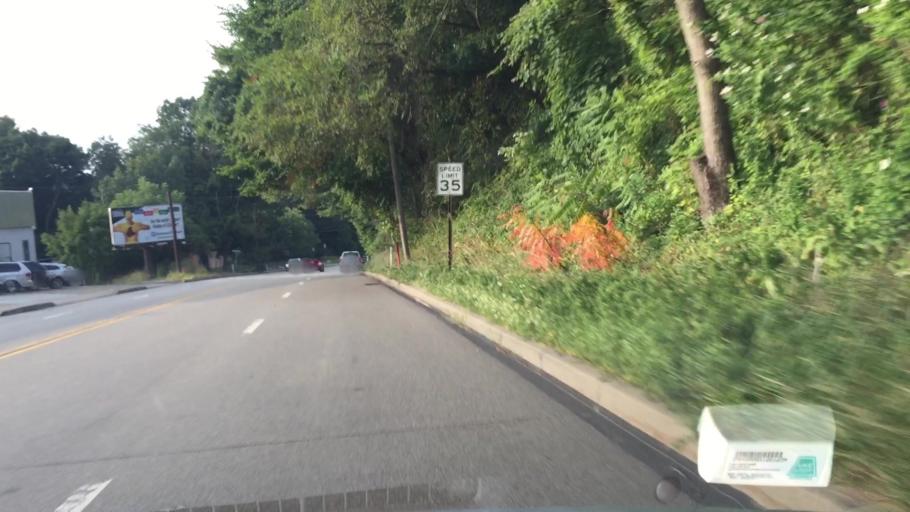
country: US
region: Pennsylvania
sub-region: Allegheny County
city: West View
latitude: 40.5515
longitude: -80.0375
